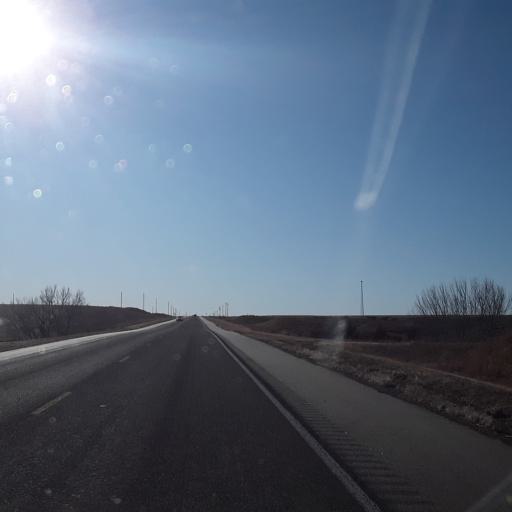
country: US
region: Nebraska
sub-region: Hitchcock County
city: Trenton
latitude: 40.2015
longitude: -100.9739
